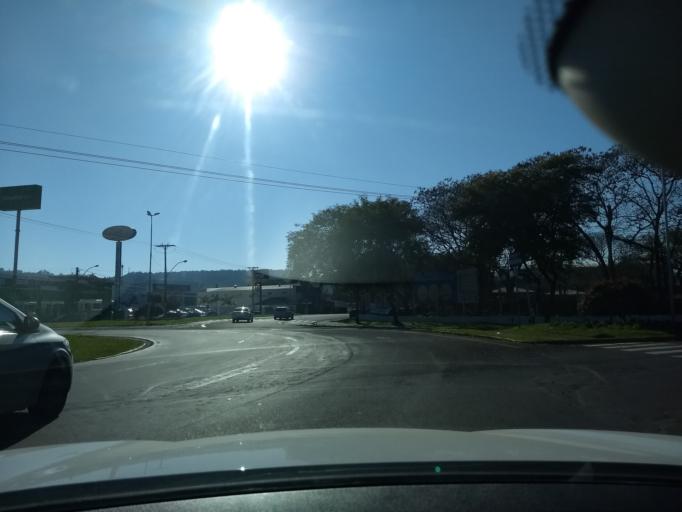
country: BR
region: Rio Grande do Sul
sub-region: Santa Cruz Do Sul
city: Santa Cruz do Sul
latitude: -29.7083
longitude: -52.4354
